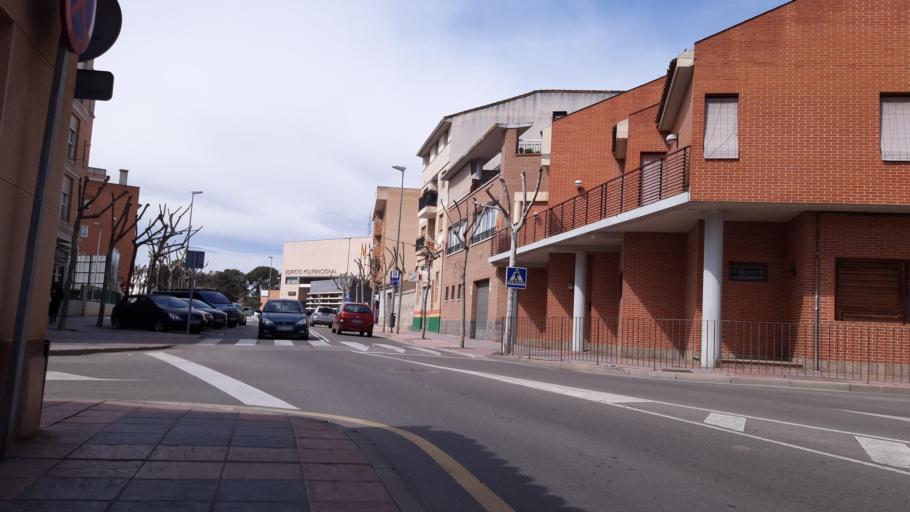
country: ES
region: Aragon
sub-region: Provincia de Zaragoza
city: Utebo
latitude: 41.7087
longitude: -0.9991
